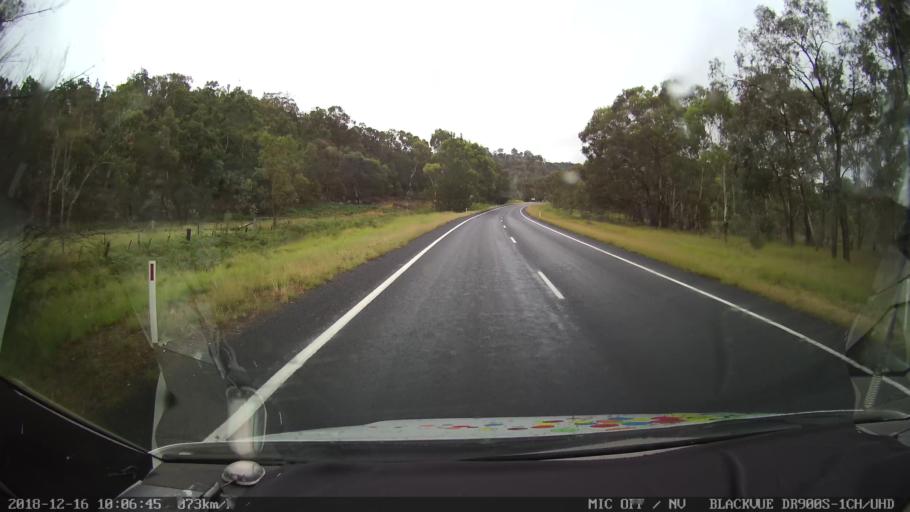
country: AU
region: New South Wales
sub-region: Glen Innes Severn
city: Glen Innes
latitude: -29.3419
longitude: 151.8924
